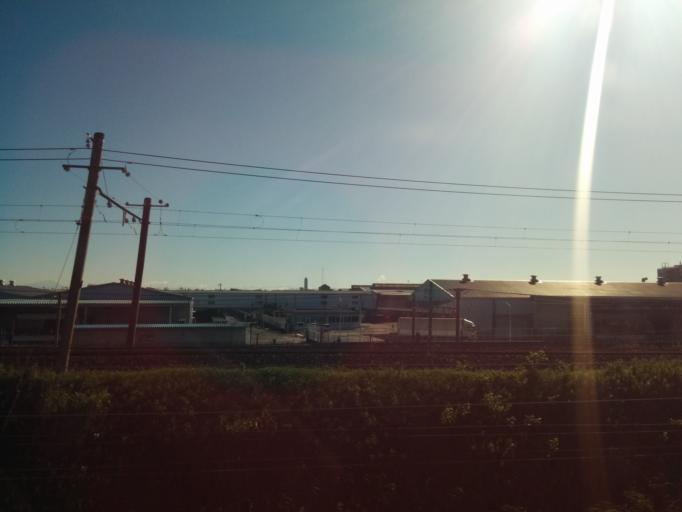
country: JP
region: Aichi
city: Nagoya-shi
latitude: 35.2102
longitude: 136.8474
